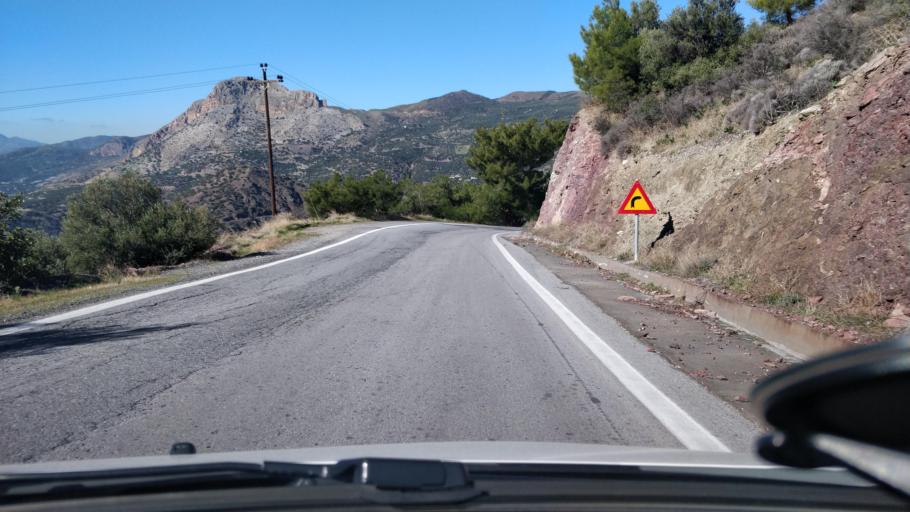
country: GR
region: Crete
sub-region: Nomos Irakleiou
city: Arkalochori
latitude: 35.0052
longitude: 25.4390
